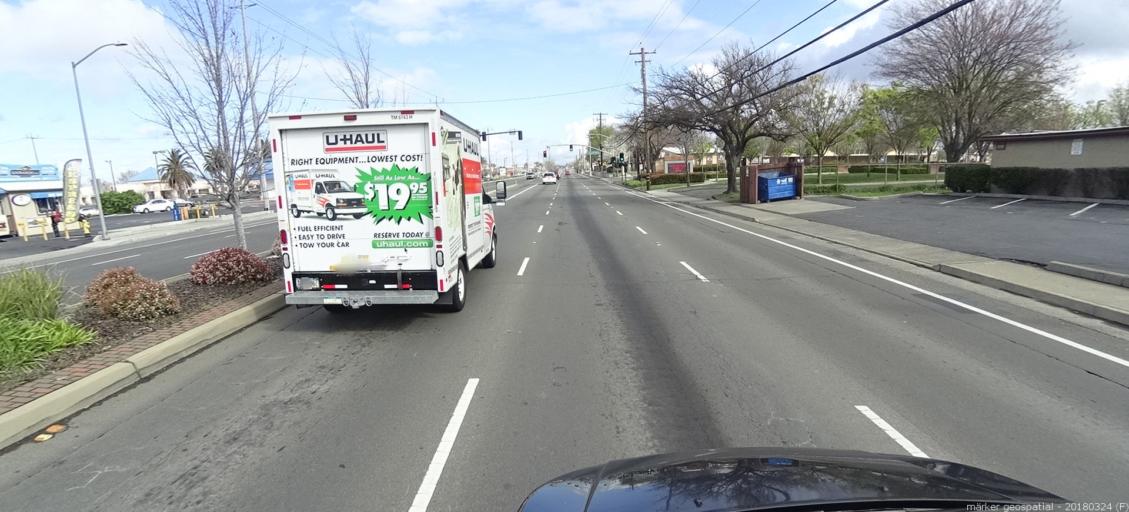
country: US
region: California
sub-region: Sacramento County
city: North Highlands
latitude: 38.6748
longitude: -121.3828
